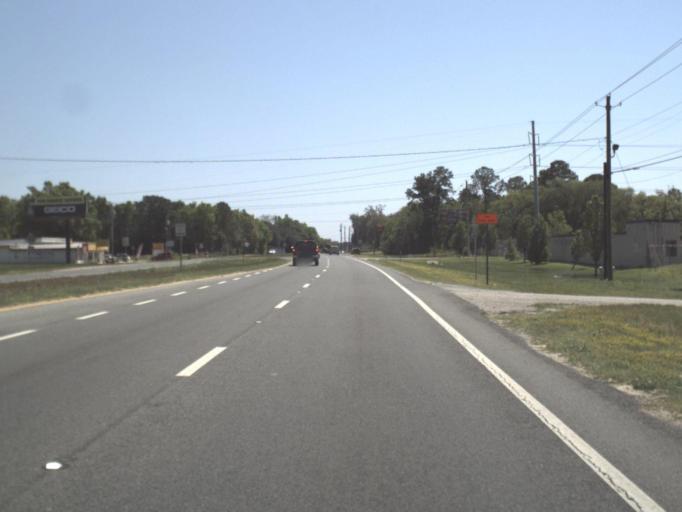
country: US
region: Florida
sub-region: Escambia County
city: Bellview
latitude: 30.4727
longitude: -87.3069
